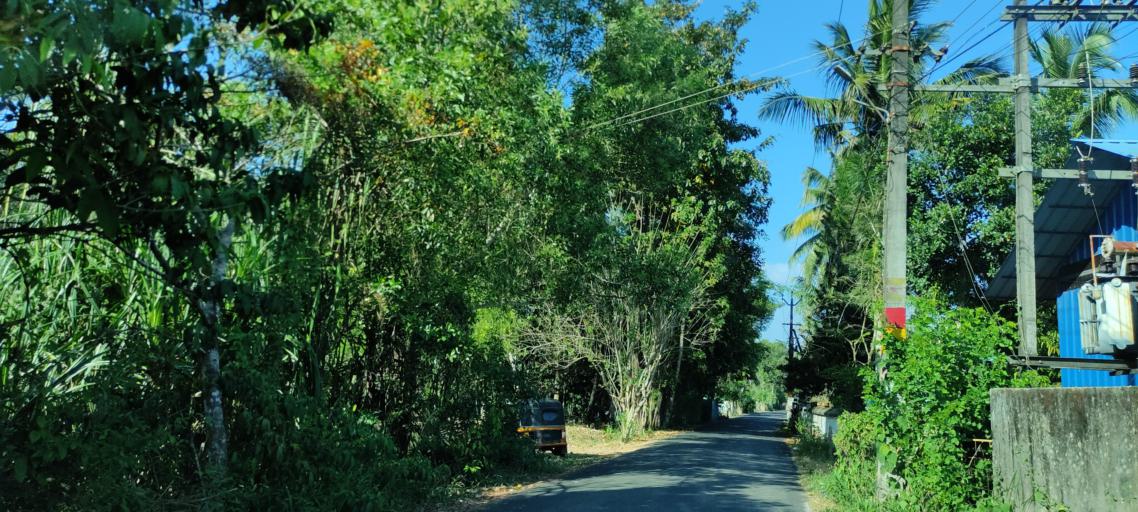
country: IN
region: Kerala
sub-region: Alappuzha
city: Shertallai
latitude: 9.6086
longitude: 76.3394
